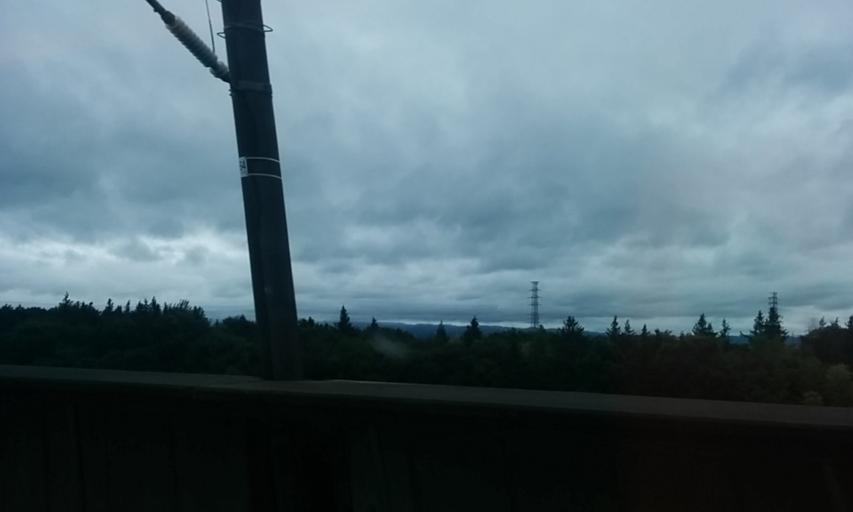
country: JP
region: Tochigi
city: Kuroiso
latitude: 36.9431
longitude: 140.0332
